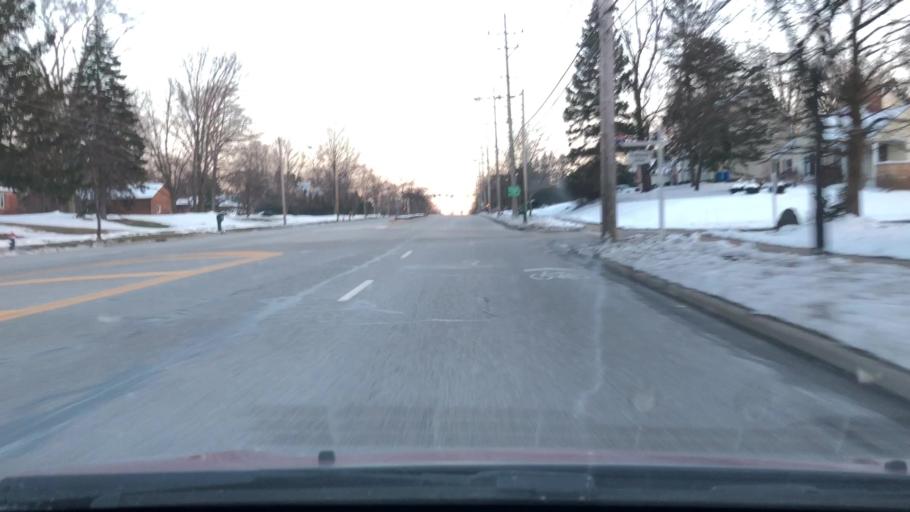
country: US
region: Ohio
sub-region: Cuyahoga County
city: Independence
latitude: 41.3605
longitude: -81.6359
